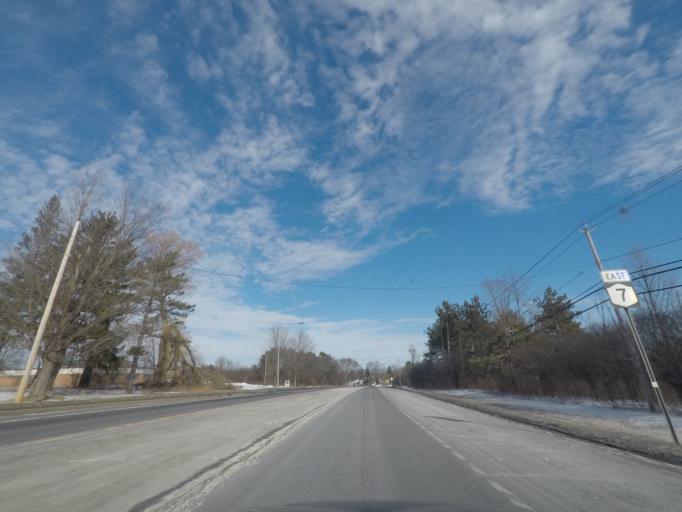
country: US
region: New York
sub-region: Schenectady County
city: Rotterdam
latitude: 42.7826
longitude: -74.0234
